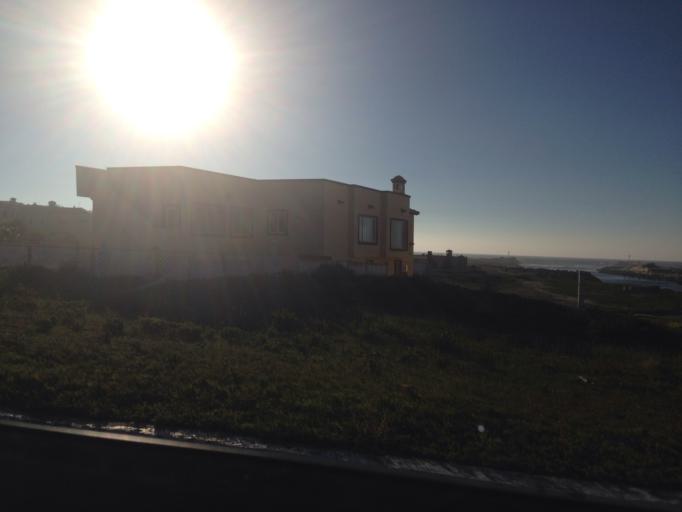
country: MX
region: Baja California
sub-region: Playas de Rosarito
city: Santa Anita
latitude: 32.0541
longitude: -116.8773
